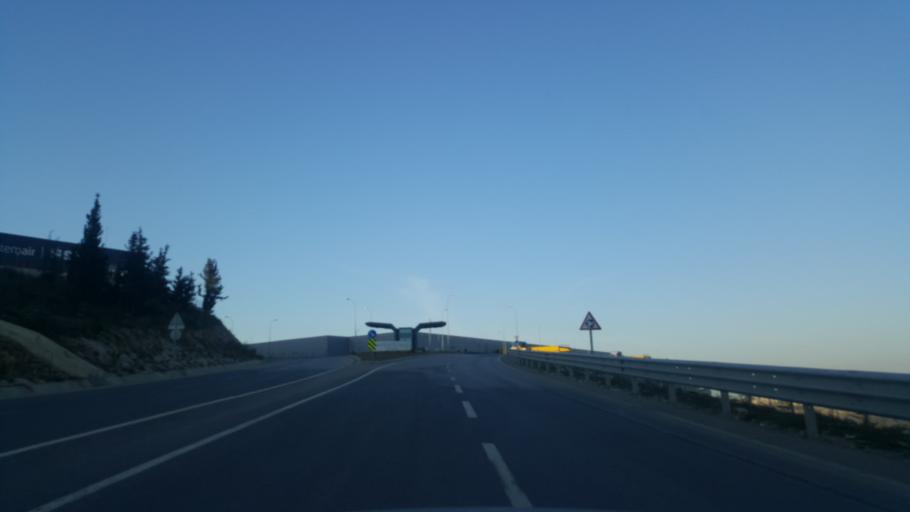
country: TR
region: Kocaeli
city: Tavsanli
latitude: 40.8387
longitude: 29.5513
